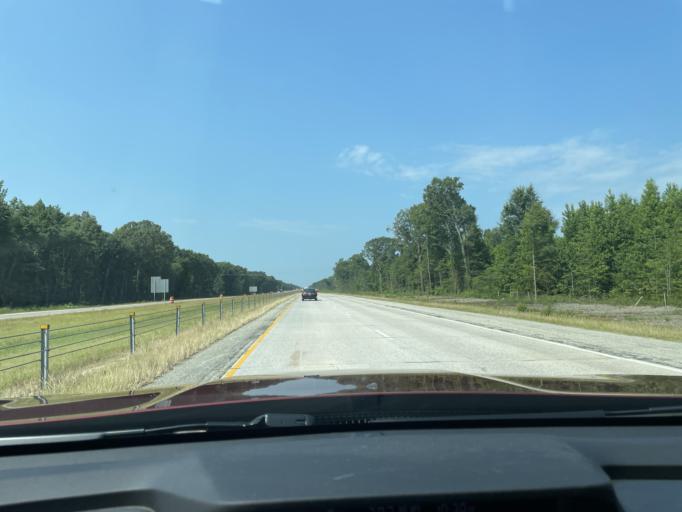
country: US
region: Arkansas
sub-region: White County
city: Searcy
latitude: 35.1911
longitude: -91.7471
